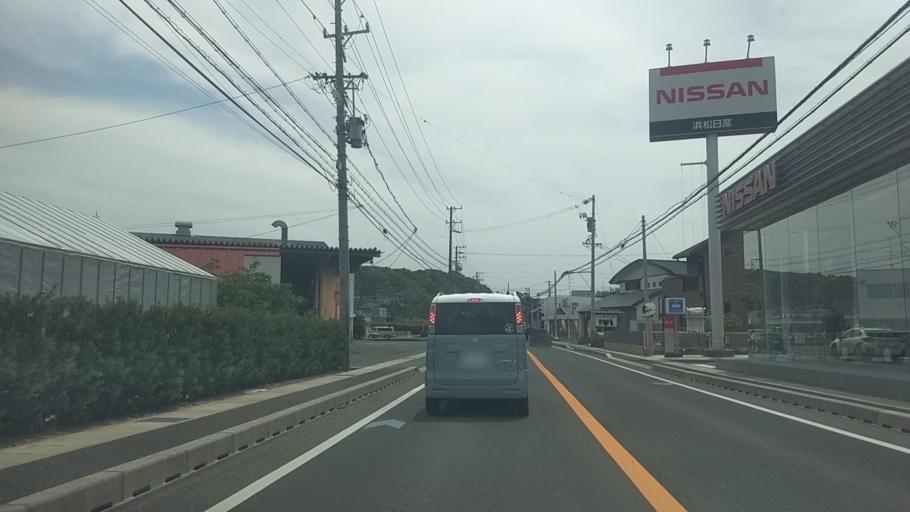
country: JP
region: Shizuoka
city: Kosai-shi
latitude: 34.7021
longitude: 137.5540
